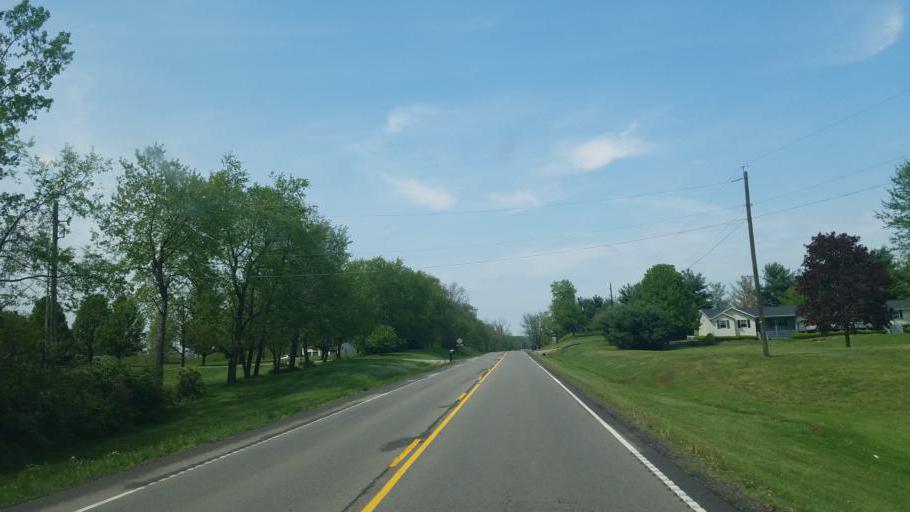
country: US
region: Ohio
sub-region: Licking County
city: Hebron
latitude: 39.9806
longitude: -82.5256
